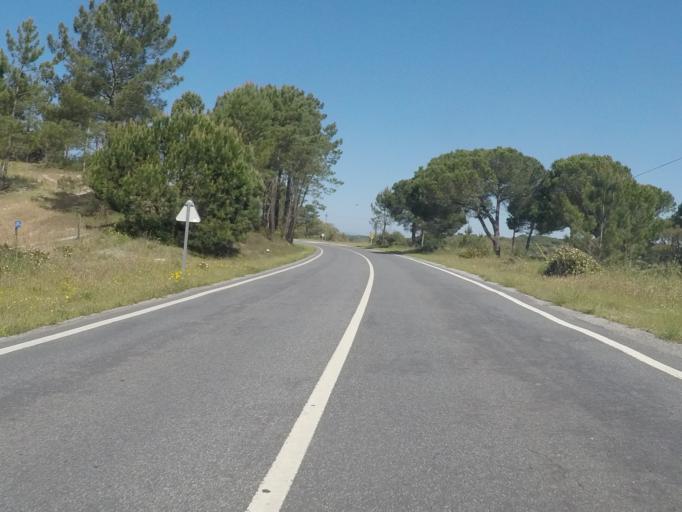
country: PT
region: Setubal
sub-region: Grandola
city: Grandola
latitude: 38.2985
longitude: -8.7258
